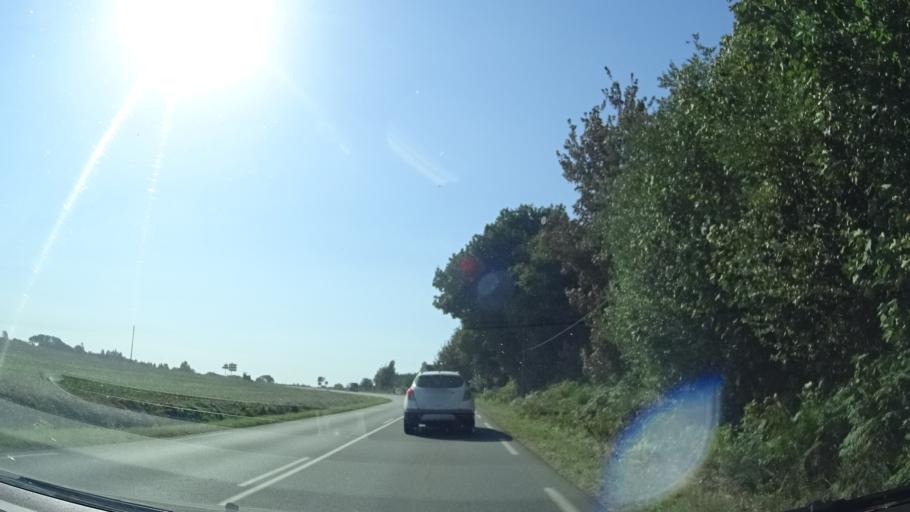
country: FR
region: Brittany
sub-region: Departement du Finistere
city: Plonevez-Porzay
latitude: 48.0950
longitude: -4.2561
